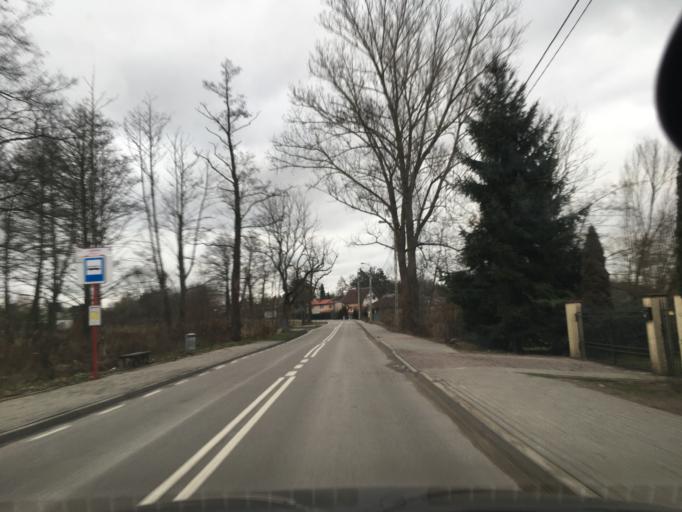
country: PL
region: Masovian Voivodeship
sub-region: Powiat piaseczynski
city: Lesznowola
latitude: 52.0394
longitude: 20.9455
